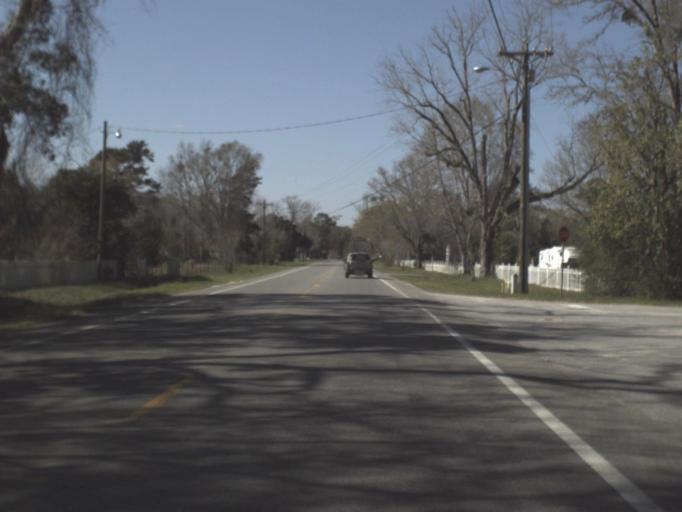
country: US
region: Florida
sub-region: Gulf County
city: Wewahitchka
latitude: 30.0959
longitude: -85.1977
